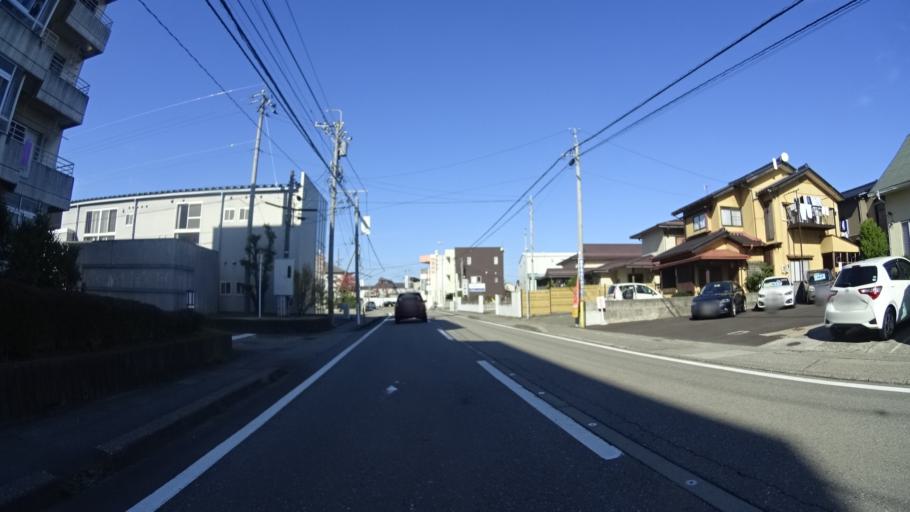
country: JP
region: Ishikawa
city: Kanazawa-shi
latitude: 36.5995
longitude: 136.6084
